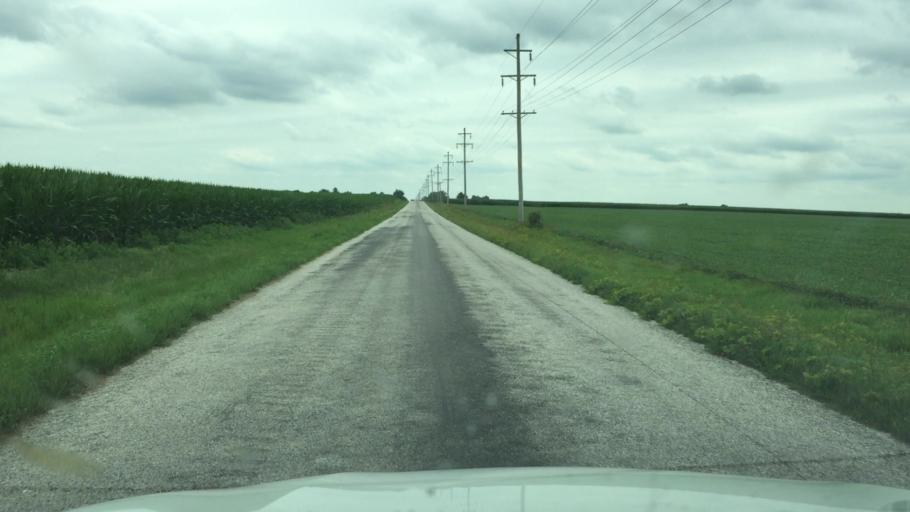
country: US
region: Illinois
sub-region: Hancock County
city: Carthage
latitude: 40.3406
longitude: -91.0823
